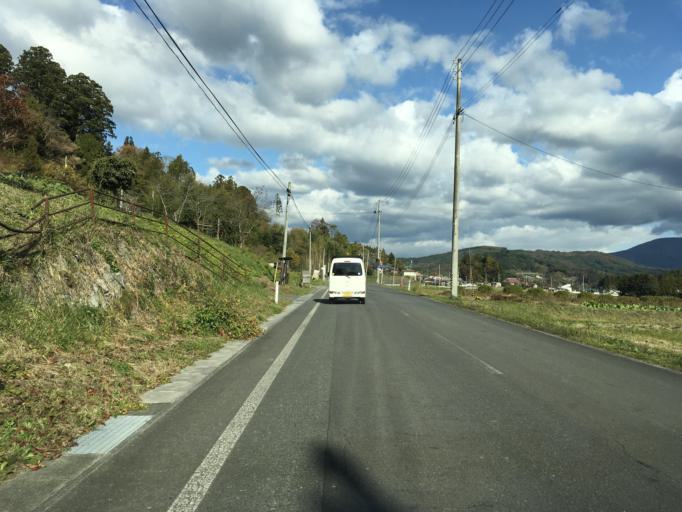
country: JP
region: Iwate
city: Ichinoseki
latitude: 38.9520
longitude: 141.3508
